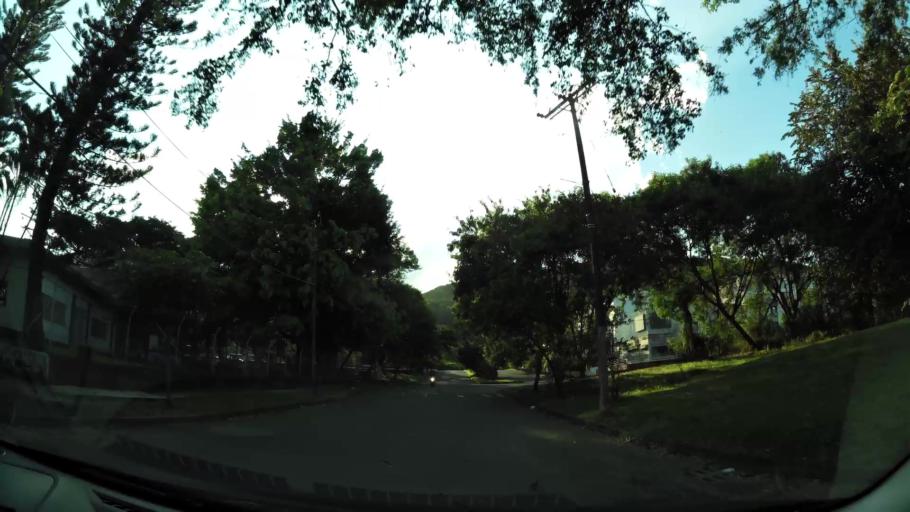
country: CO
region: Valle del Cauca
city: Cali
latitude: 3.4019
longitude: -76.5551
